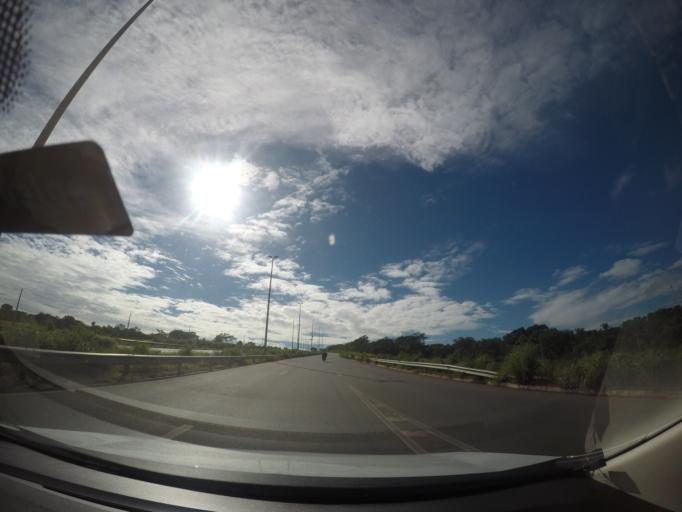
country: BR
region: Goias
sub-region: Goiania
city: Goiania
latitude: -16.6879
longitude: -49.1836
